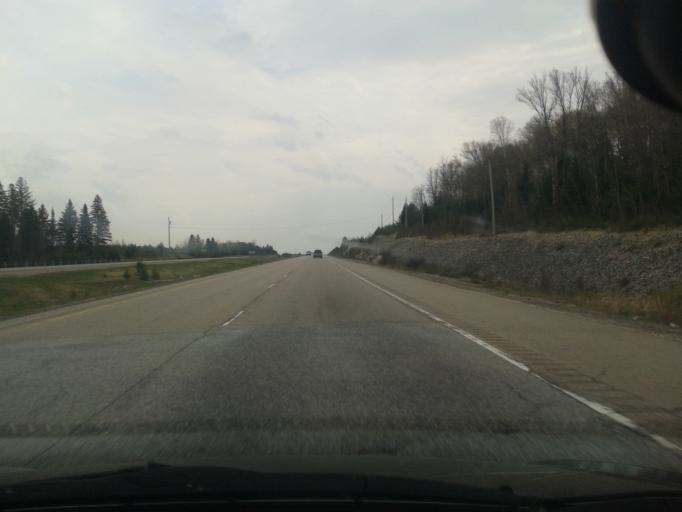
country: CA
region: Ontario
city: Powassan
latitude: 45.9559
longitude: -79.3642
